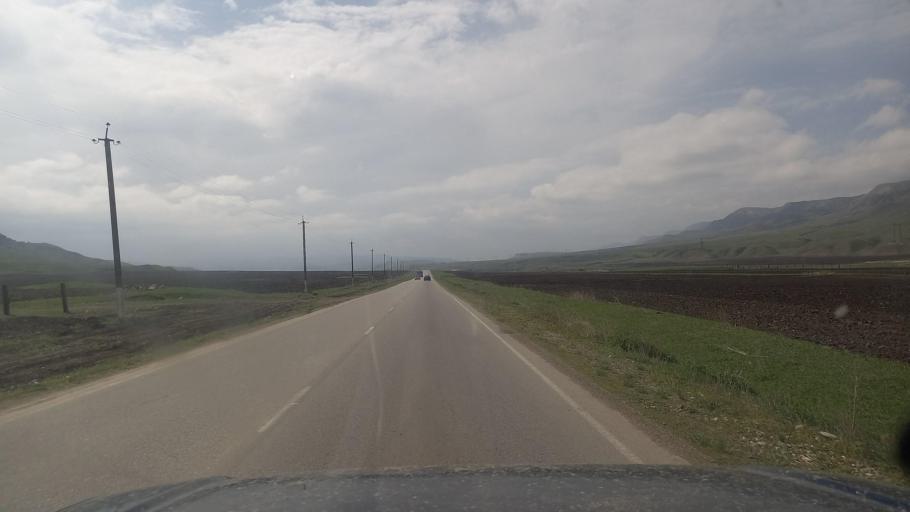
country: RU
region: Kabardino-Balkariya
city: Kamennomostskoye
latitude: 43.7262
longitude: 43.1142
